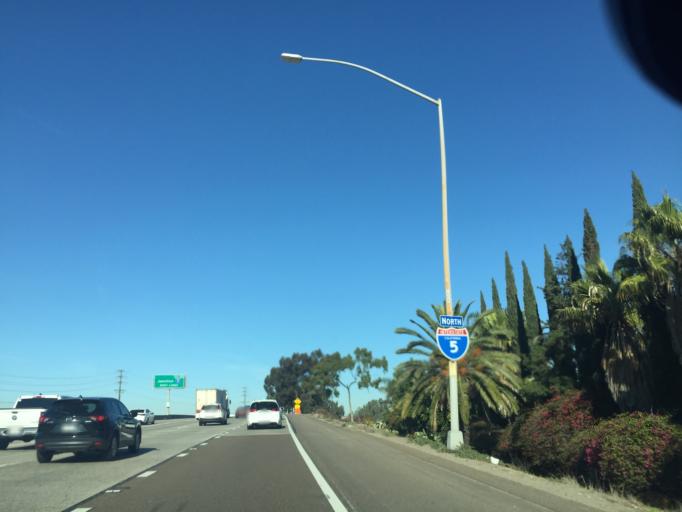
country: US
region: California
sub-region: San Diego County
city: San Diego
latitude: 32.7511
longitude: -117.1969
